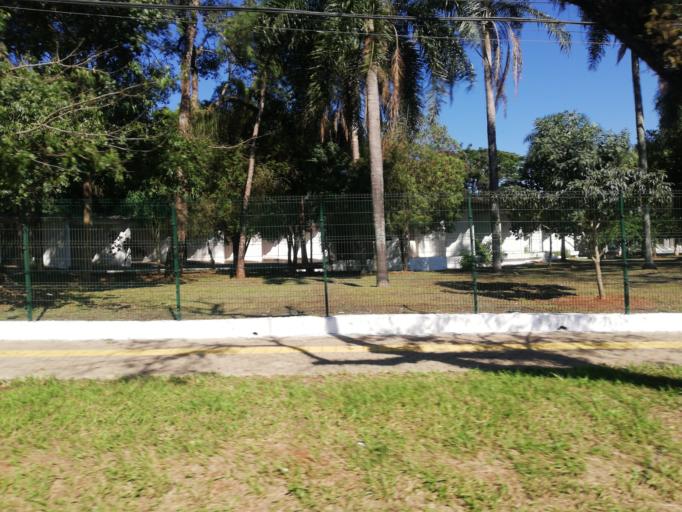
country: BR
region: Parana
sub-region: Foz Do Iguacu
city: Foz do Iguacu
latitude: -25.5567
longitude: -54.5644
